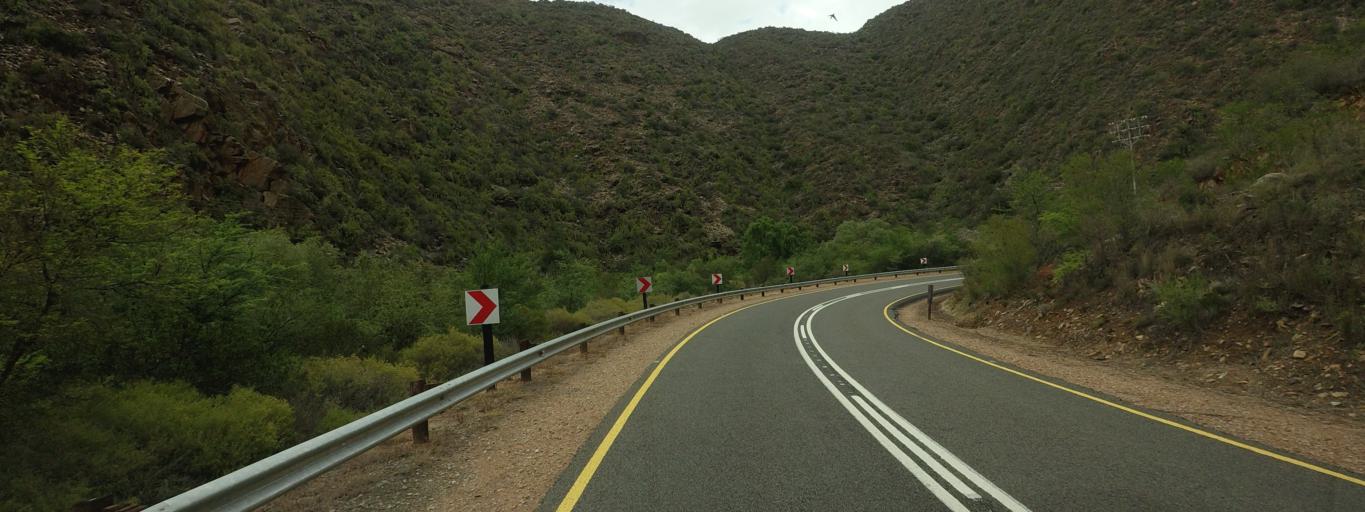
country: ZA
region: Western Cape
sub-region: Eden District Municipality
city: Oudtshoorn
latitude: -33.4268
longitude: 22.2477
